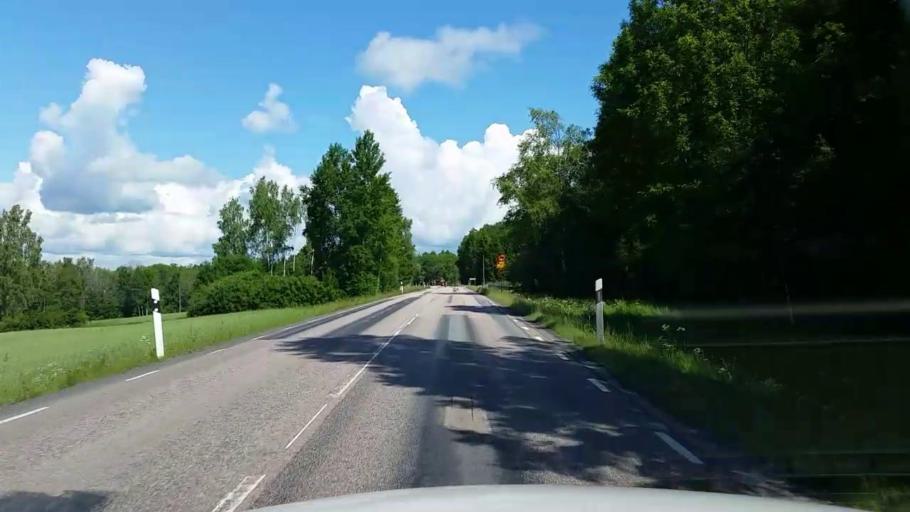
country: SE
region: Vaestmanland
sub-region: Kopings Kommun
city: Kolsva
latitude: 59.6205
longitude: 15.8207
